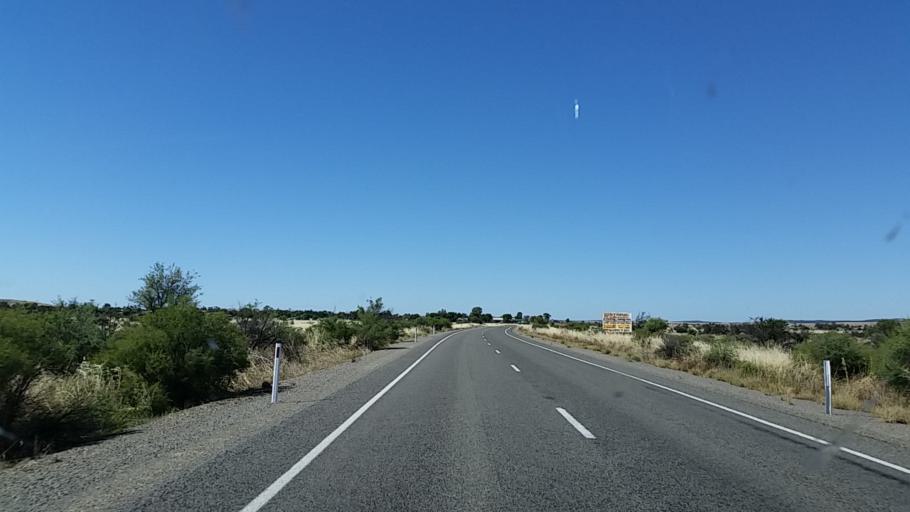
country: AU
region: South Australia
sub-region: Peterborough
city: Peterborough
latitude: -33.1607
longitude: 138.9178
